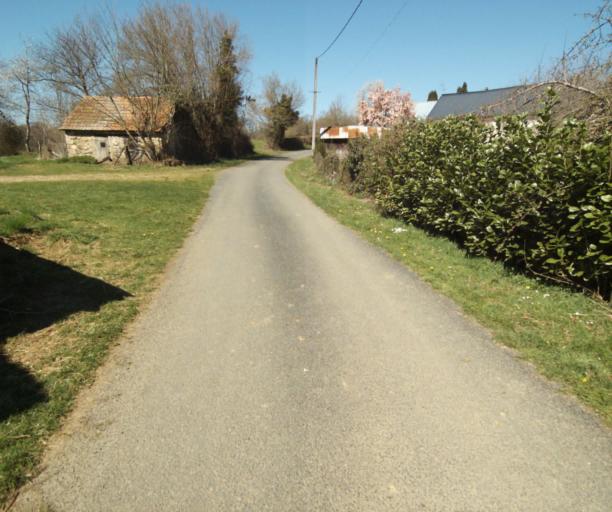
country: FR
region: Limousin
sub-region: Departement de la Correze
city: Saint-Clement
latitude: 45.3221
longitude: 1.6936
